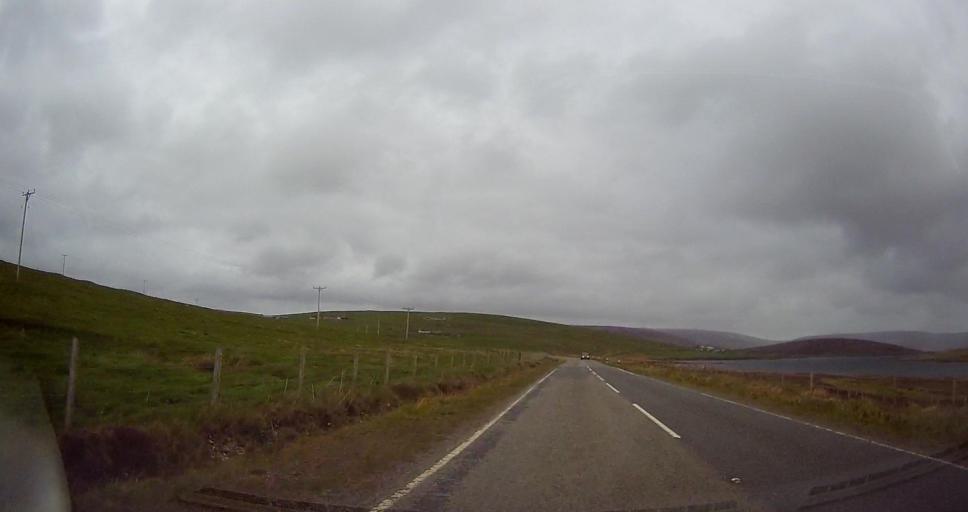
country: GB
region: Scotland
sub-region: Shetland Islands
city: Lerwick
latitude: 60.2566
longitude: -1.4301
